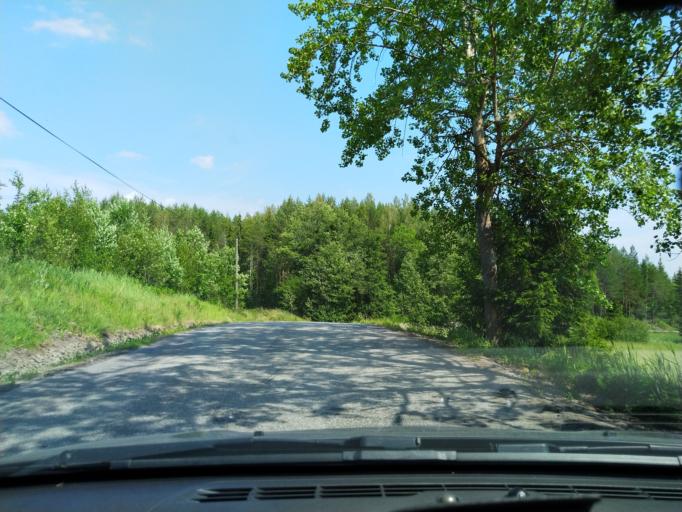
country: FI
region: Uusimaa
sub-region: Helsinki
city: Lohja
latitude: 60.3427
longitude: 24.0763
